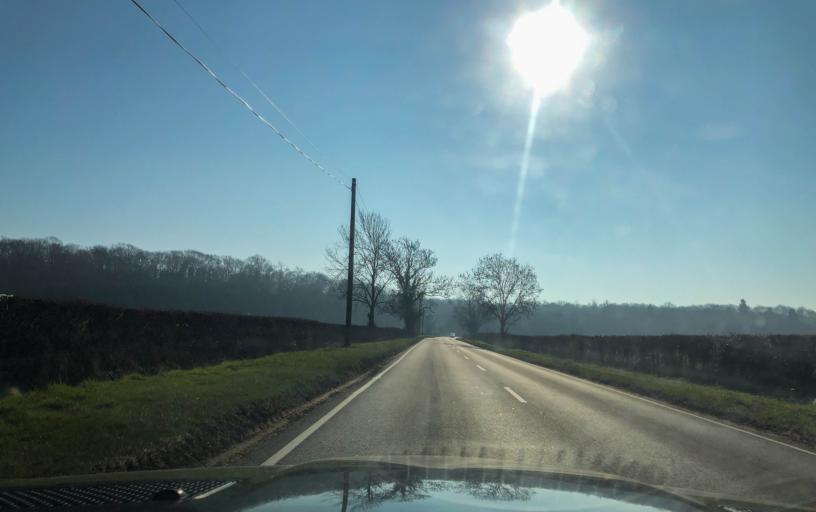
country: GB
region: England
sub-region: Warwickshire
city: Wellesbourne Mountford
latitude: 52.1834
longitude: -1.5760
